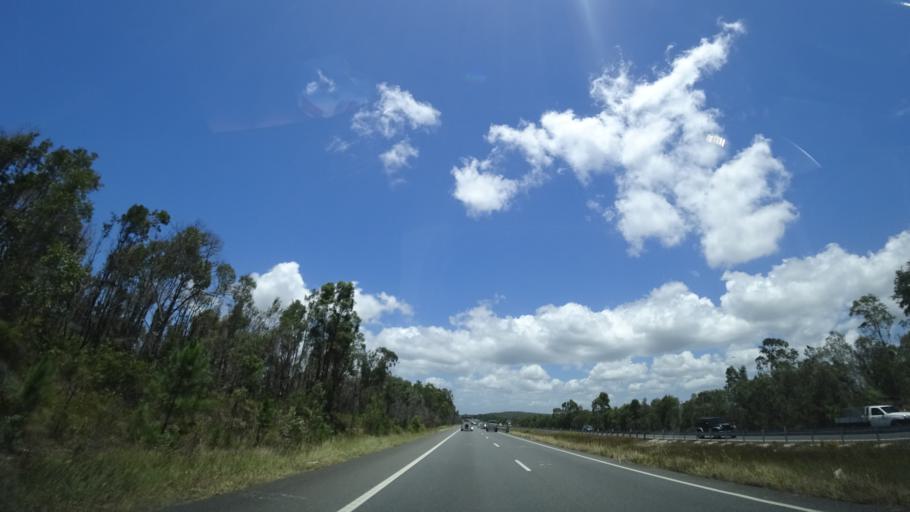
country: AU
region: Queensland
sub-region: Sunshine Coast
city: Little Mountain
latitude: -26.7978
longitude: 153.0434
